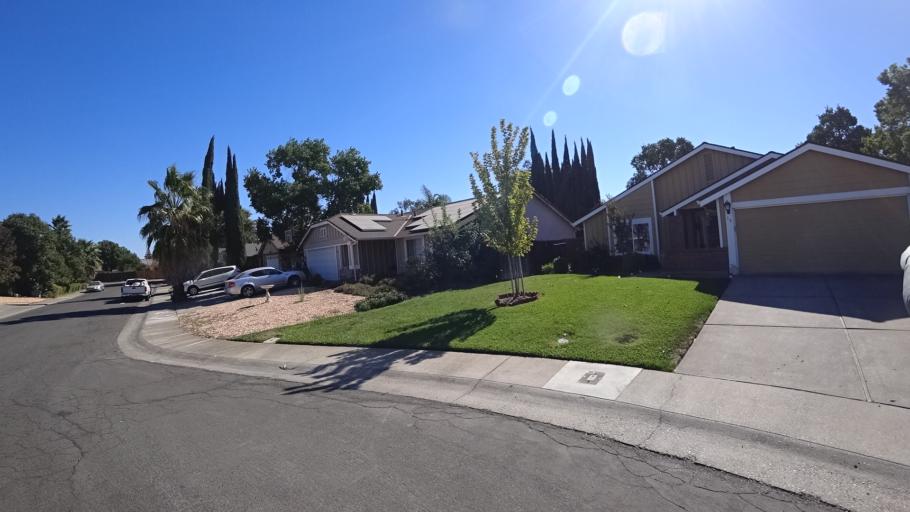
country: US
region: California
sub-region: Sacramento County
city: Parkway
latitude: 38.4669
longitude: -121.4612
